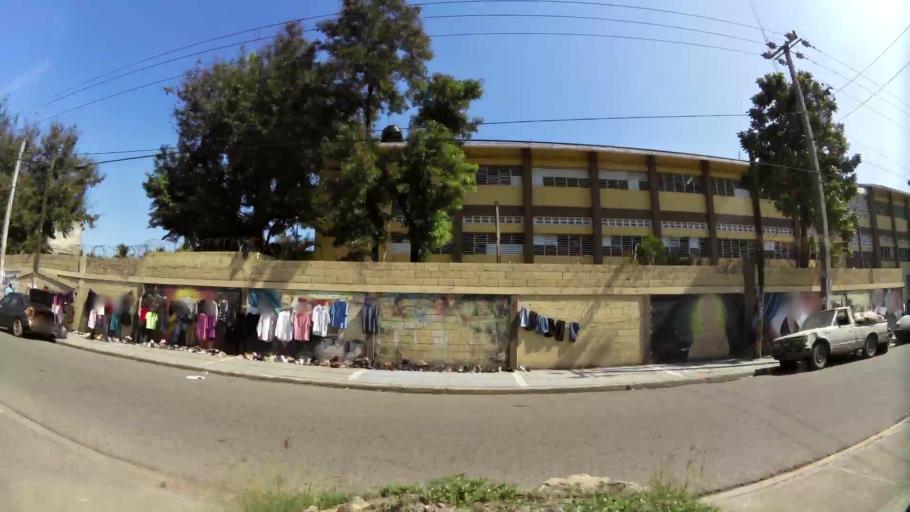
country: DO
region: Santo Domingo
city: Santo Domingo Oeste
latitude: 18.4833
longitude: -69.9996
